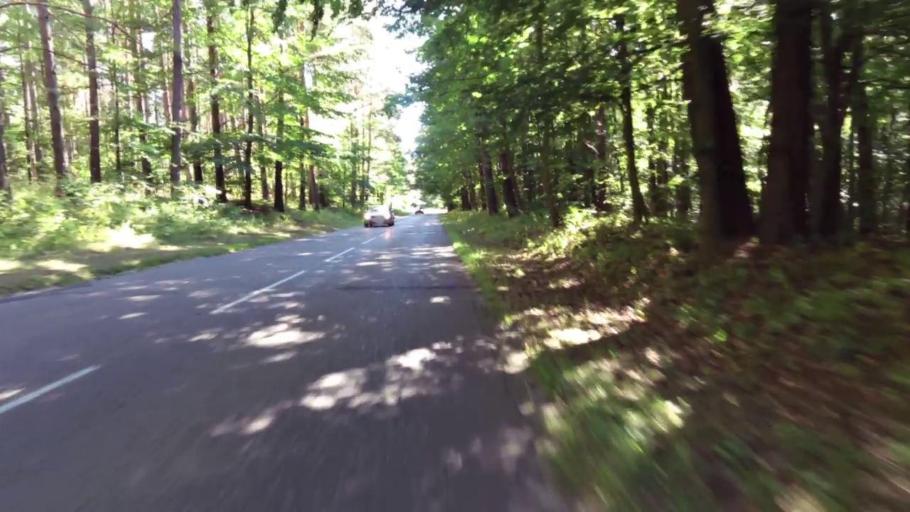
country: PL
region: West Pomeranian Voivodeship
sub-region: Powiat szczecinecki
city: Borne Sulinowo
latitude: 53.5864
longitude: 16.5743
